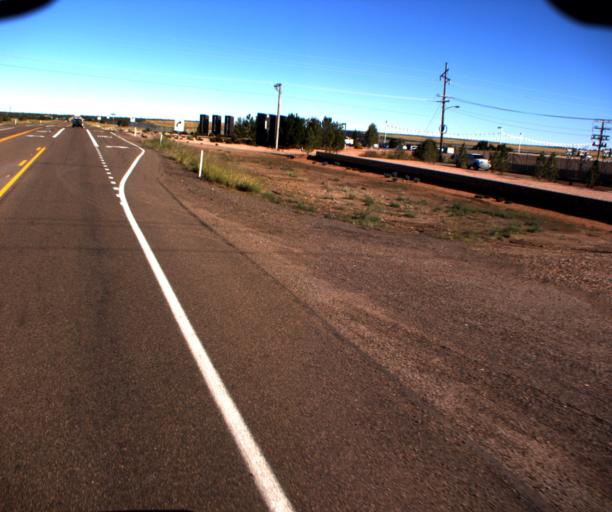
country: US
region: Arizona
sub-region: Navajo County
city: Show Low
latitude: 34.2601
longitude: -110.0192
